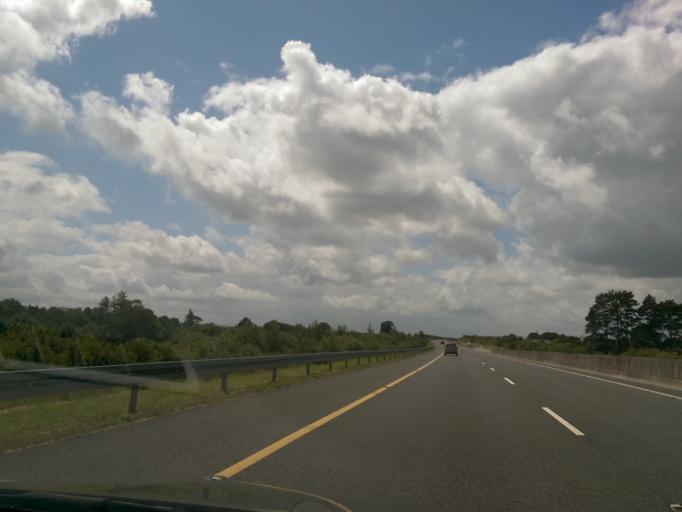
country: IE
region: Munster
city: Cahir
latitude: 52.3390
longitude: -8.0229
